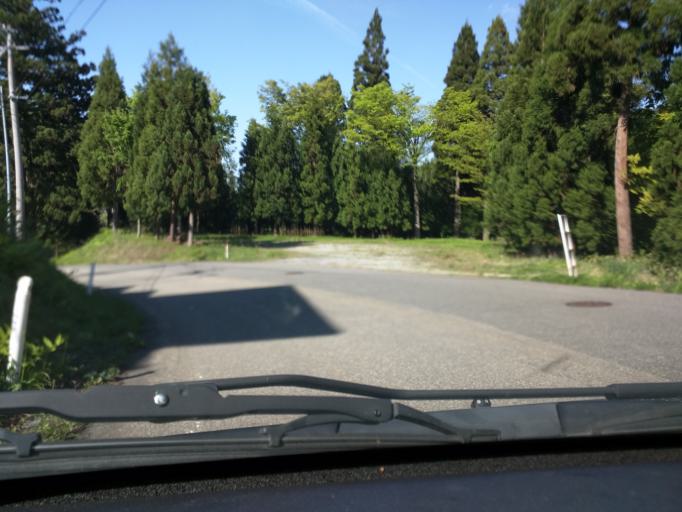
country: JP
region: Fukushima
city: Kitakata
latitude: 37.5603
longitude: 139.6268
